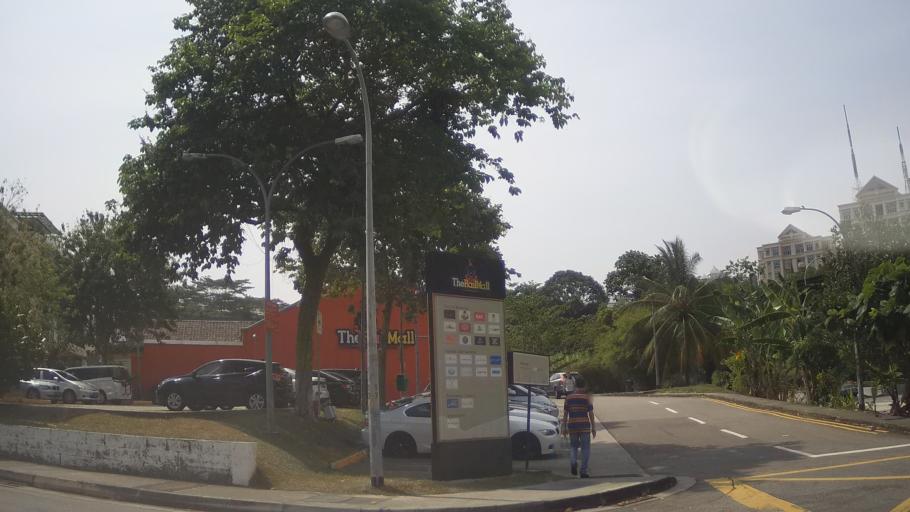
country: MY
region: Johor
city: Johor Bahru
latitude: 1.3586
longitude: 103.7676
